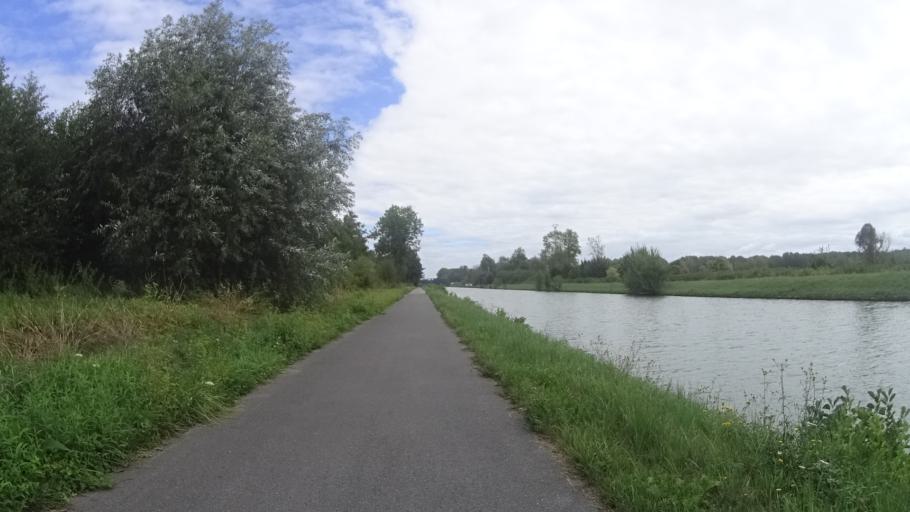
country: FR
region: Picardie
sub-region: Departement de l'Oise
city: Noyon
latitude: 49.5646
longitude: 3.0183
